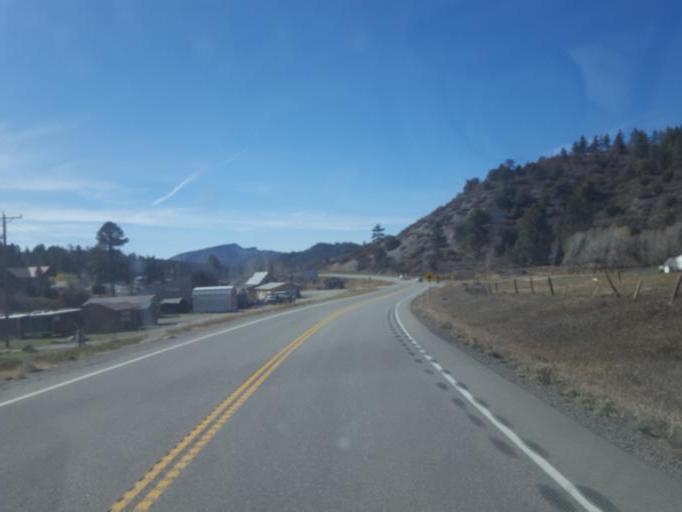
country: US
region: Colorado
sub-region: Archuleta County
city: Pagosa Springs
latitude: 37.2390
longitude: -107.1557
